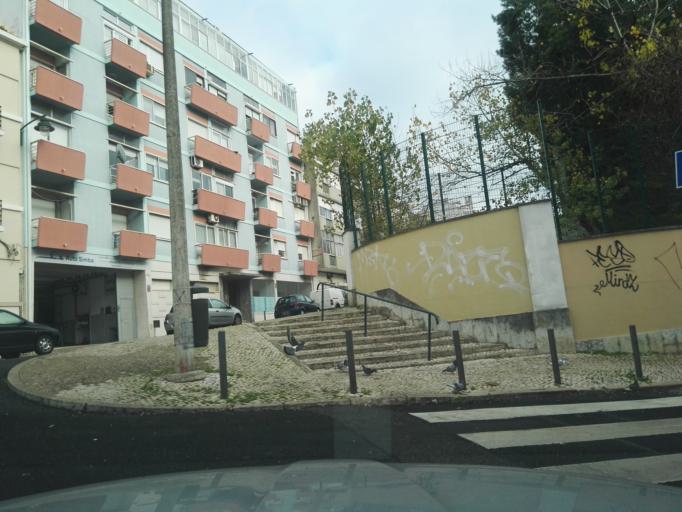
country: PT
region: Lisbon
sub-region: Lisbon
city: Lisbon
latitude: 38.7405
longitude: -9.1302
